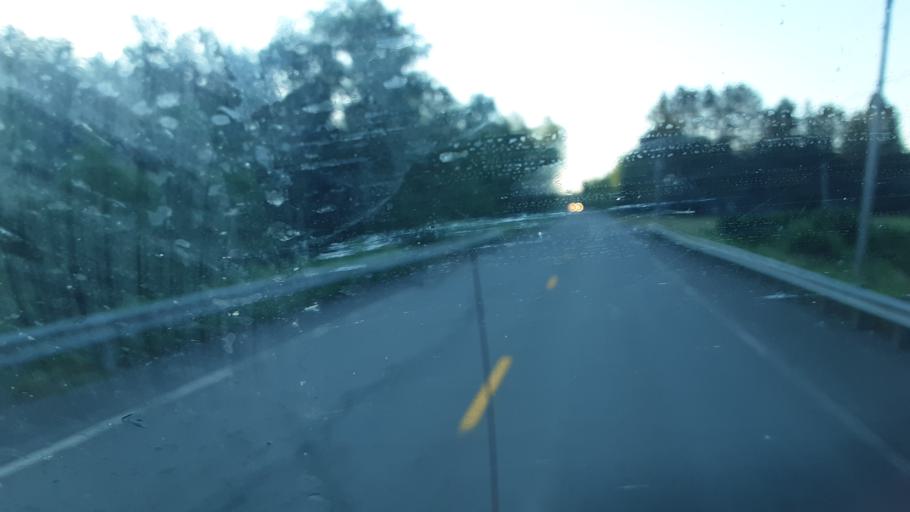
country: US
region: Maine
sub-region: Aroostook County
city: Presque Isle
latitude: 46.7535
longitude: -68.0574
